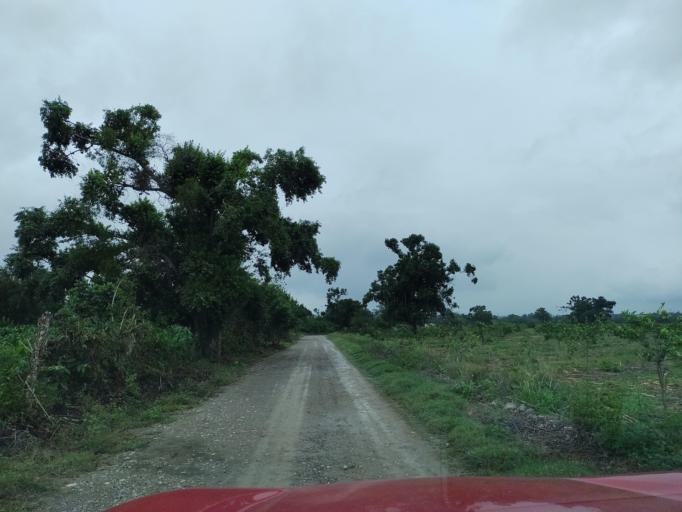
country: MX
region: Veracruz
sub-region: Papantla
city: El Chote
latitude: 20.3951
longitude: -97.3139
